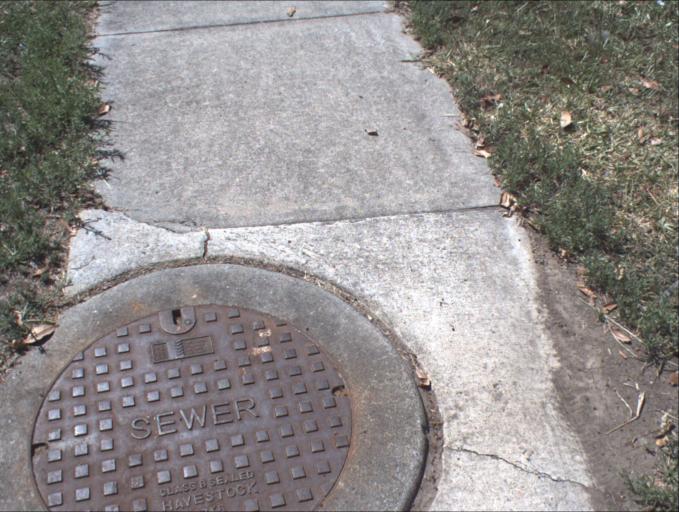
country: AU
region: Queensland
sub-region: Gold Coast
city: Yatala
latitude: -27.6928
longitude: 153.2188
